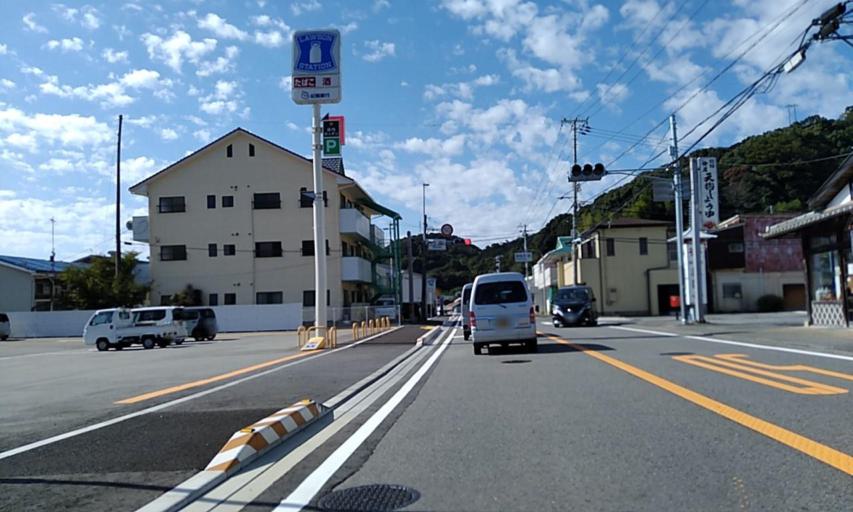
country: JP
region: Wakayama
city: Gobo
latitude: 33.9707
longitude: 135.1296
